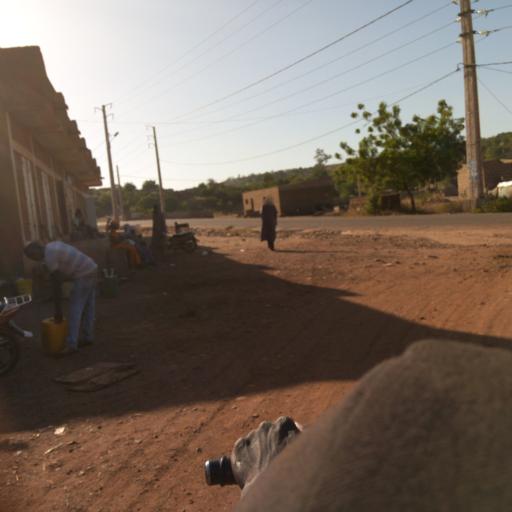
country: ML
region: Bamako
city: Bamako
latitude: 12.6556
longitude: -8.0405
